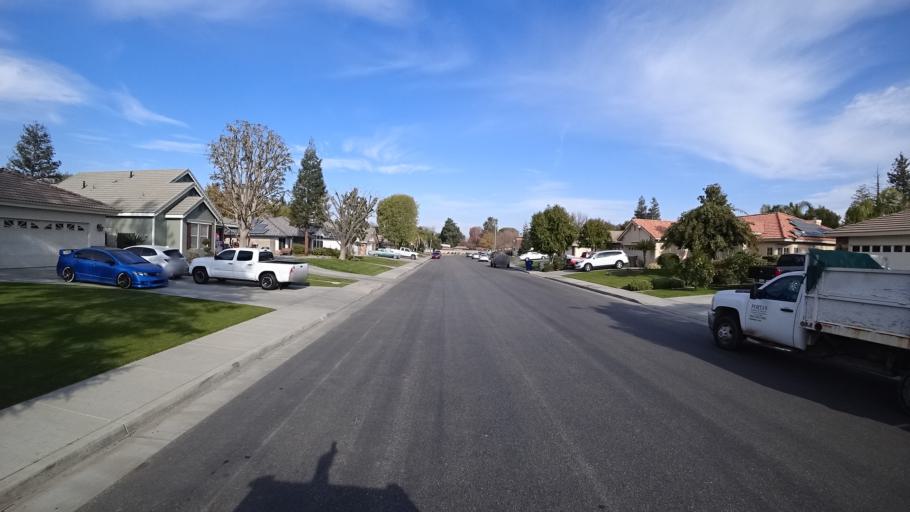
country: US
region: California
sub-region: Kern County
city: Greenacres
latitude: 35.4087
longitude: -119.0695
